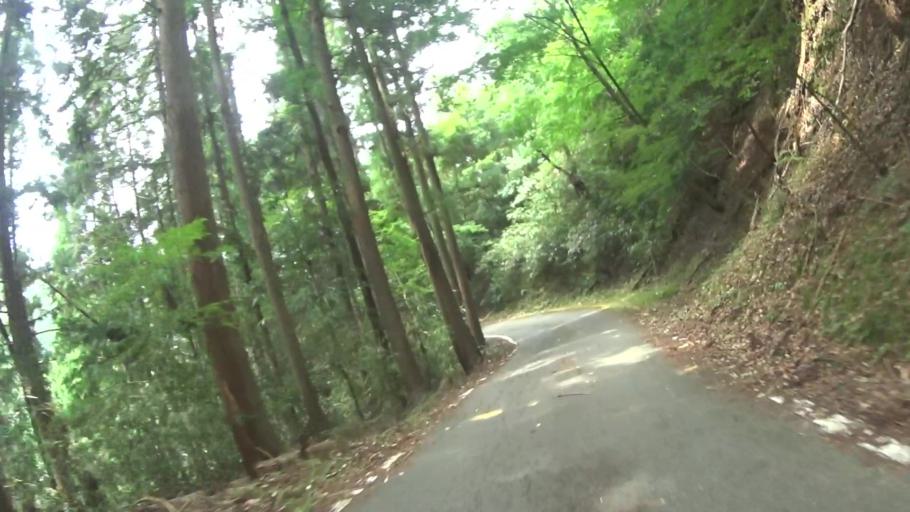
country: JP
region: Kyoto
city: Kameoka
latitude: 35.2006
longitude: 135.5830
